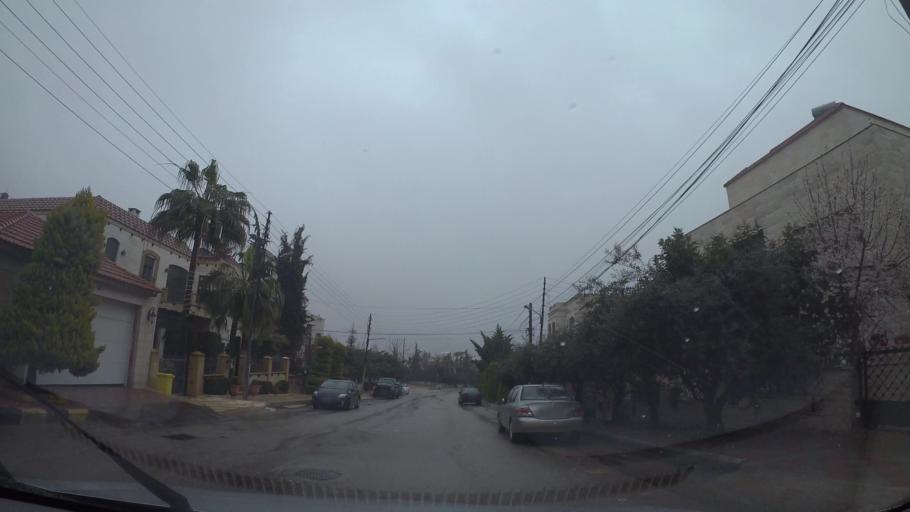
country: JO
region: Amman
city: Wadi as Sir
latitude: 31.9966
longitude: 35.8228
